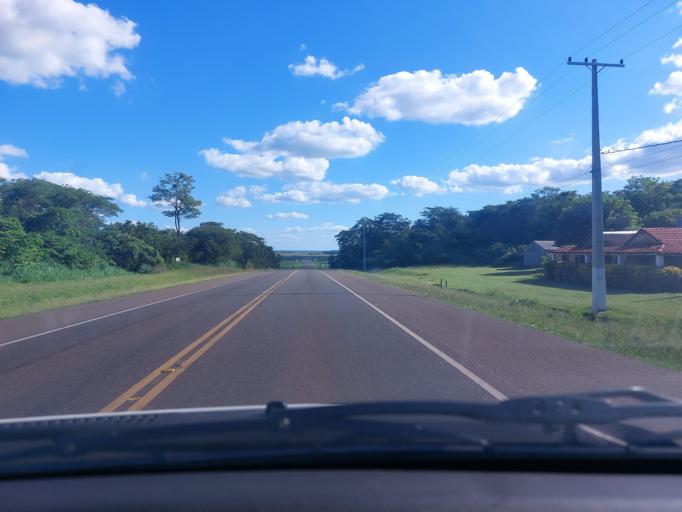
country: PY
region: San Pedro
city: Union
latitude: -24.7654
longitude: -56.6803
